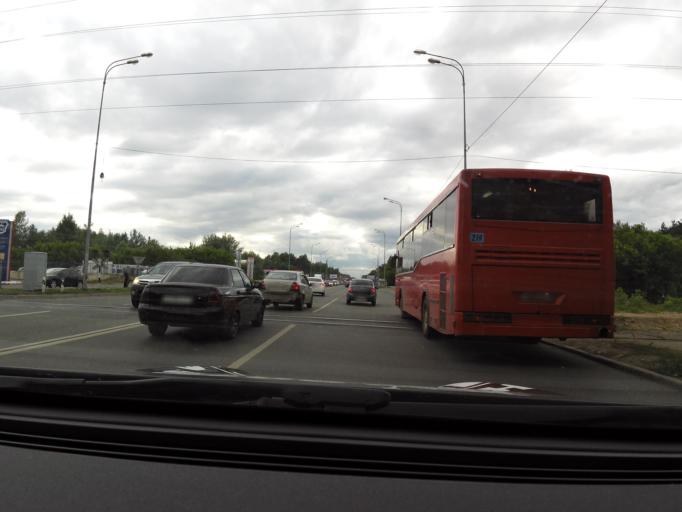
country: RU
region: Tatarstan
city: Staroye Arakchino
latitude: 55.8271
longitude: 49.0236
